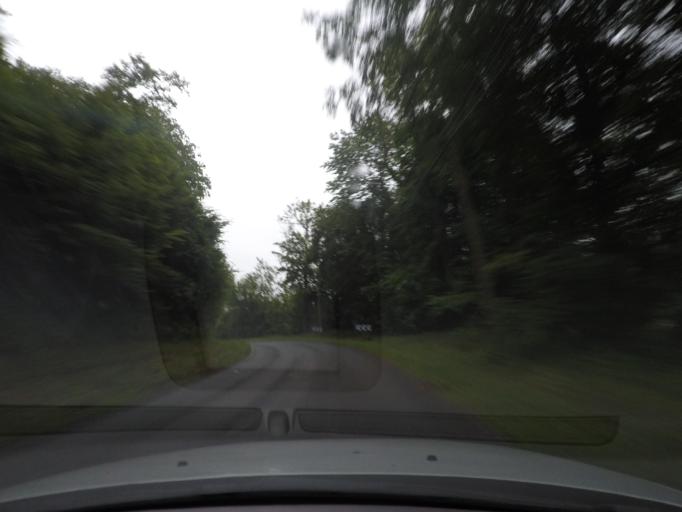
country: FR
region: Haute-Normandie
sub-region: Departement de la Seine-Maritime
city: Fontaine-le-Bourg
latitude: 49.5789
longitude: 1.2186
